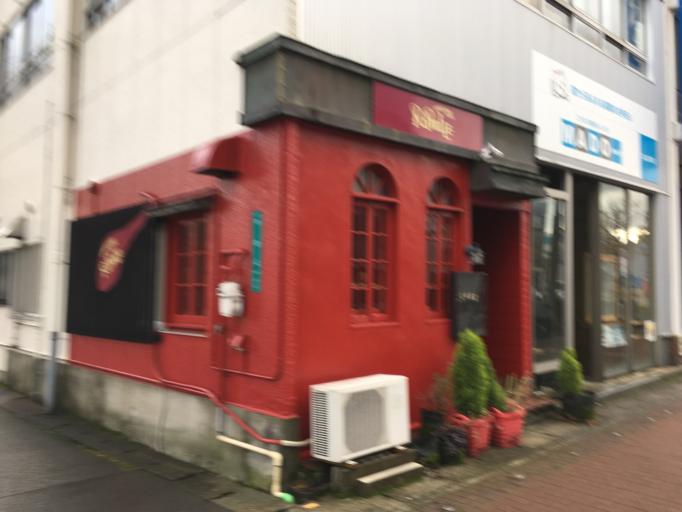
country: JP
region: Toyama
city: Toyama-shi
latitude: 36.6937
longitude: 137.2158
